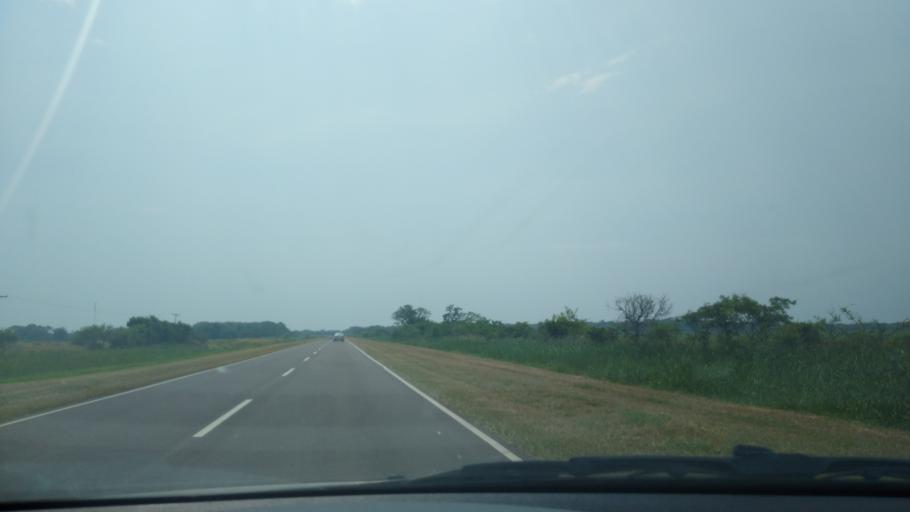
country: AR
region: Chaco
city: La Eduvigis
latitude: -26.8481
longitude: -59.0494
